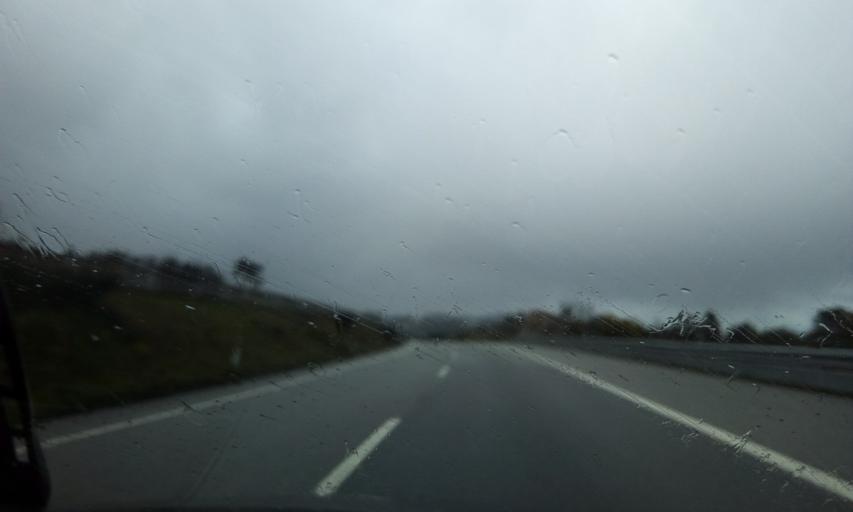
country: PT
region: Viseu
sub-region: Mangualde
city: Mangualde
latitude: 40.6140
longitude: -7.7018
